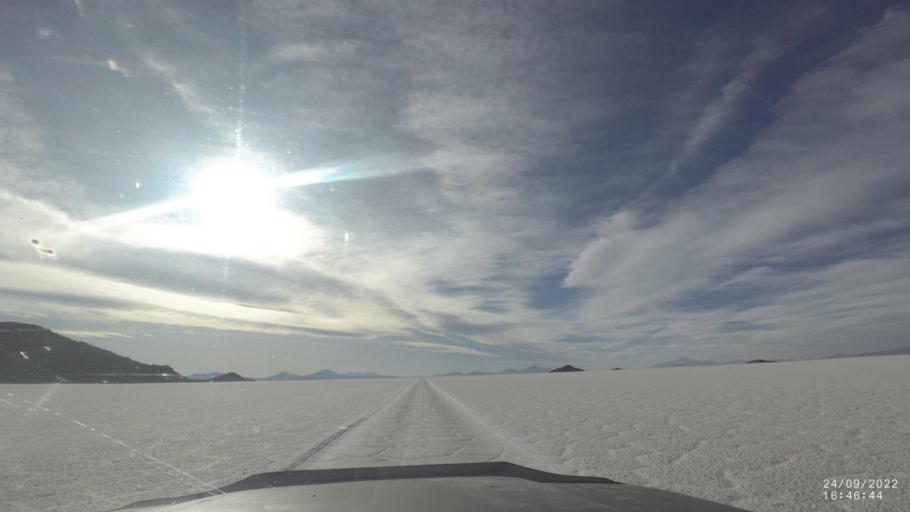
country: BO
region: Potosi
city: Colchani
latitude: -20.1353
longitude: -67.7945
